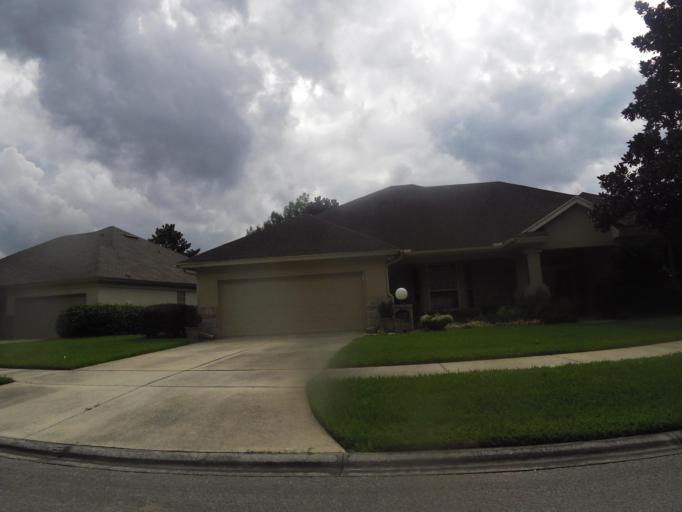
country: US
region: Florida
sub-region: Duval County
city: Jacksonville Beach
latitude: 30.2617
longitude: -81.4544
